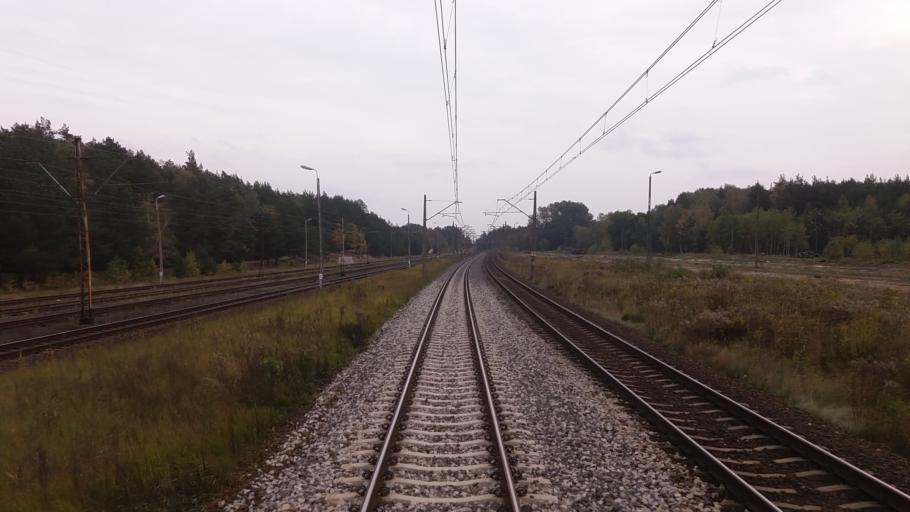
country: PL
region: West Pomeranian Voivodeship
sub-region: Powiat gryfinski
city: Stare Czarnowo
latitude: 53.3901
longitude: 14.7021
